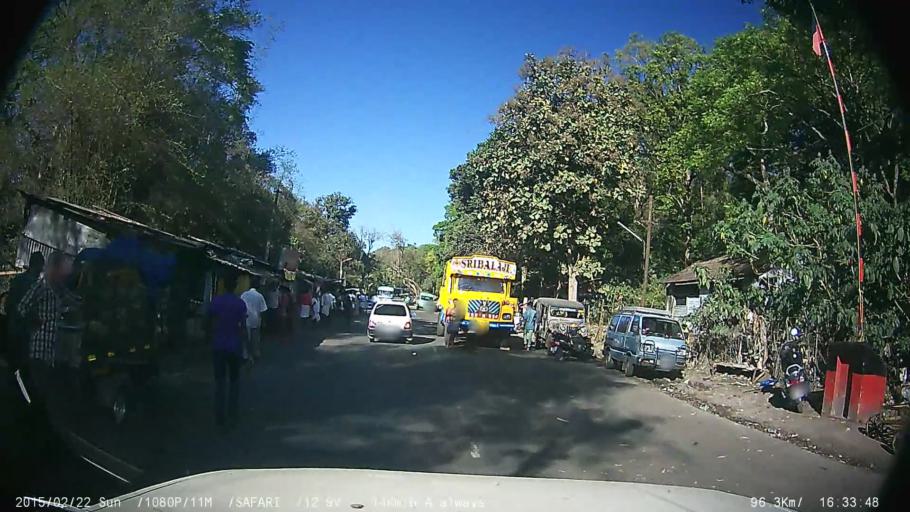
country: IN
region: Tamil Nadu
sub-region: Theni
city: Gudalur
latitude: 9.6095
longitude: 77.1700
